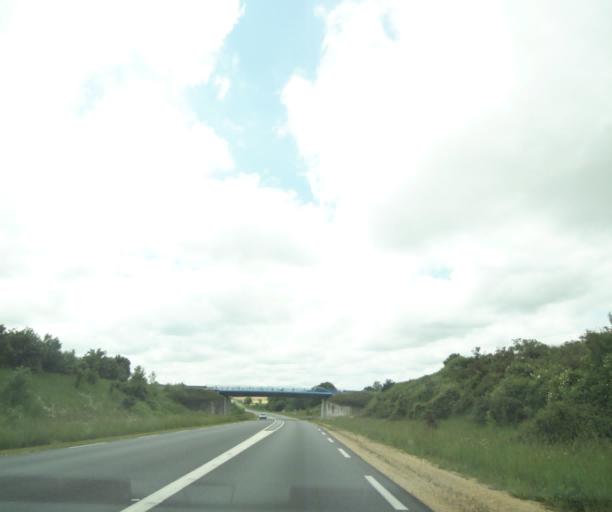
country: FR
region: Poitou-Charentes
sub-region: Departement des Deux-Sevres
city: Parthenay
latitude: 46.6532
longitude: -0.2681
